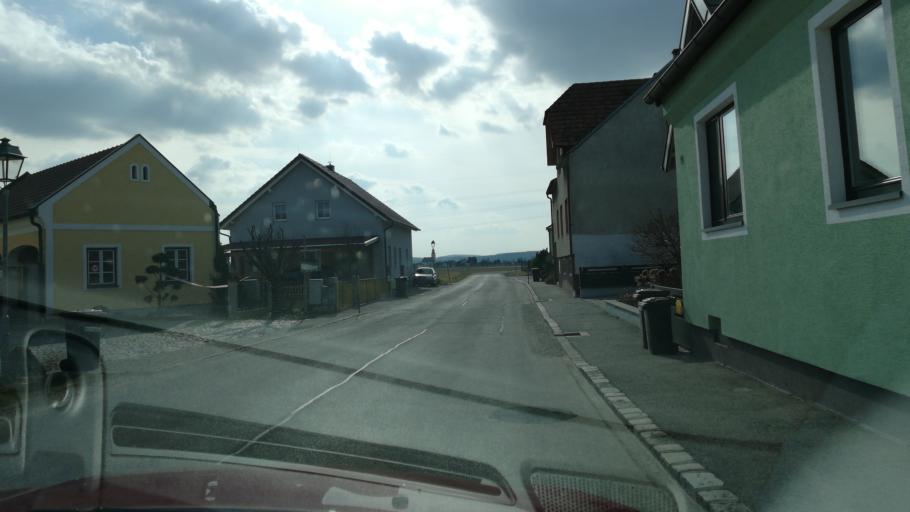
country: AT
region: Lower Austria
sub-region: Politischer Bezirk Tulln
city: Langenrohr
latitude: 48.3161
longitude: 16.0122
